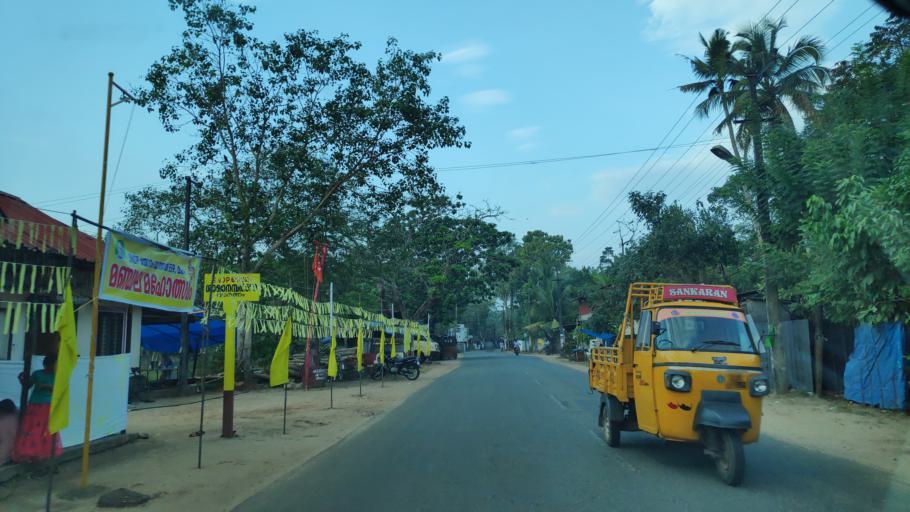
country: IN
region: Kerala
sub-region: Alappuzha
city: Shertallai
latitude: 9.6464
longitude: 76.3710
